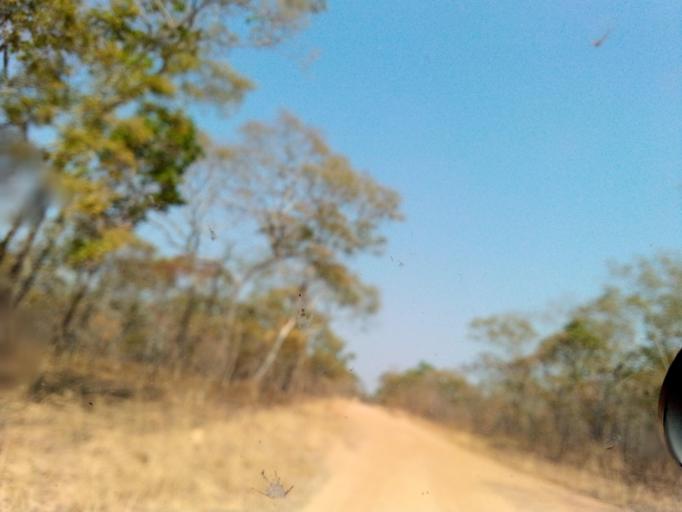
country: ZM
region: Northern
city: Mpika
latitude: -12.2418
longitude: 30.8275
